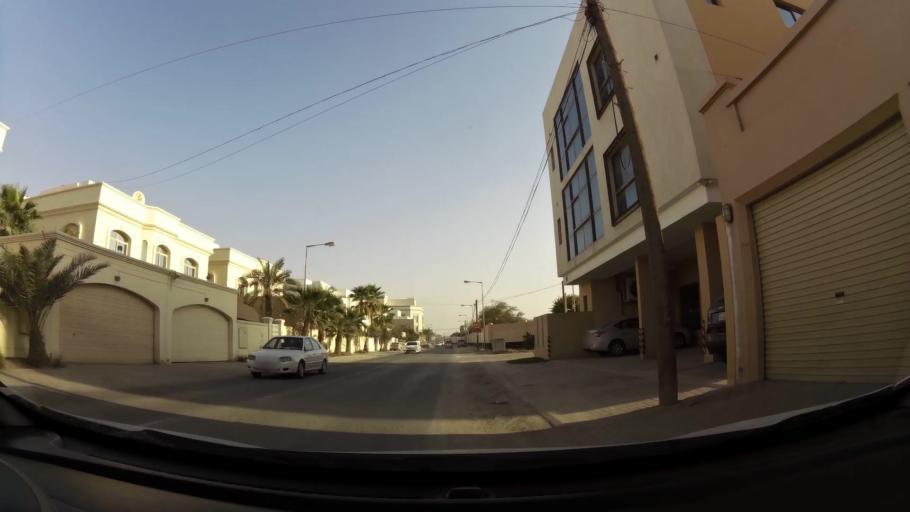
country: BH
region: Manama
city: Jidd Hafs
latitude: 26.2074
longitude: 50.4997
